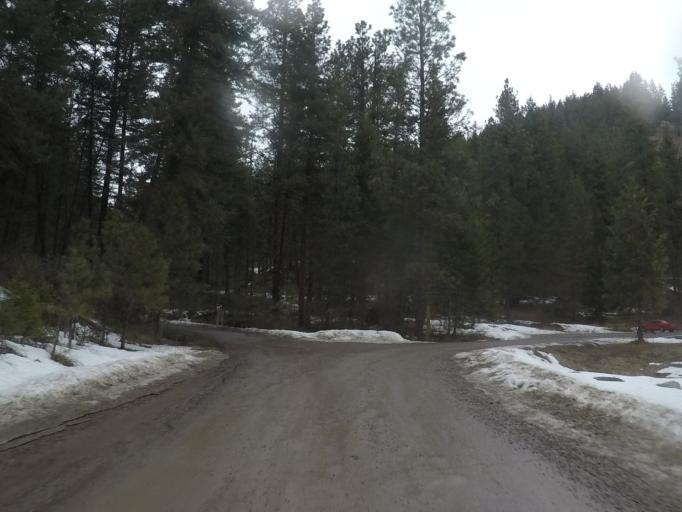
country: US
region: Montana
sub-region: Missoula County
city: East Missoula
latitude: 46.9243
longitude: -113.9616
